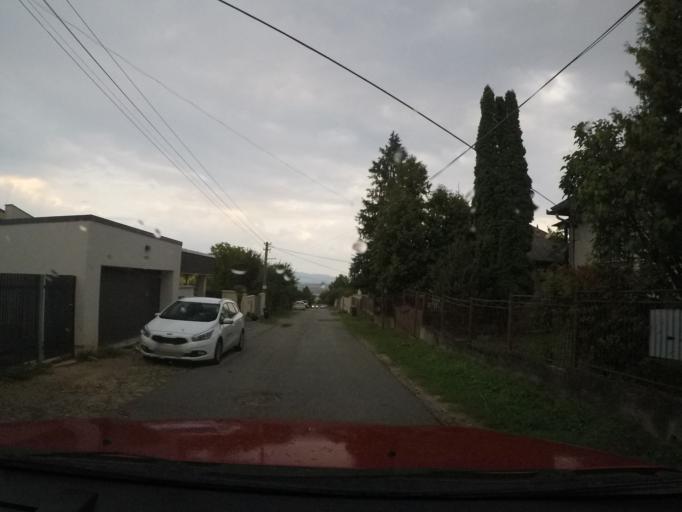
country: SK
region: Kosicky
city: Kosice
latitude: 48.6887
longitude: 21.2156
